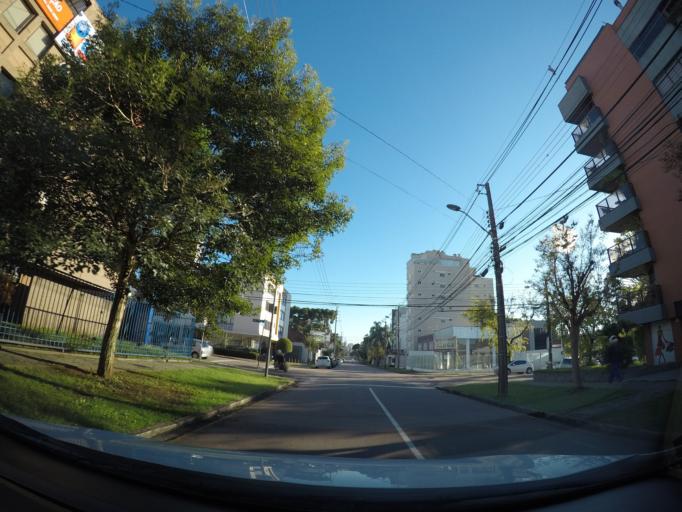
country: BR
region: Parana
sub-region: Curitiba
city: Curitiba
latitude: -25.4256
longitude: -49.2560
